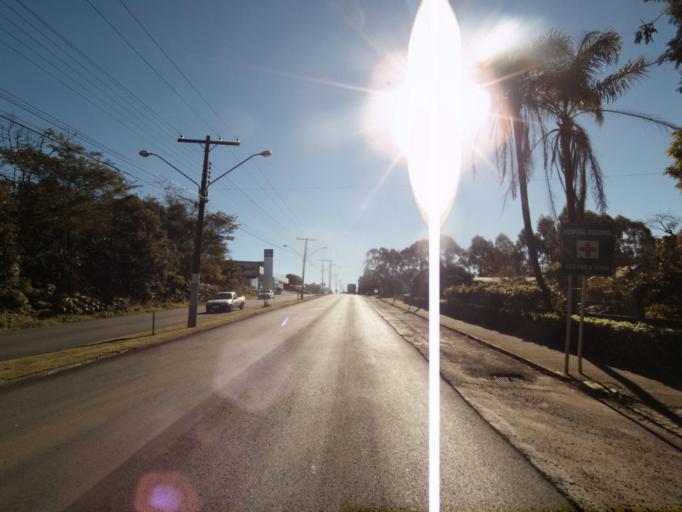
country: AR
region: Misiones
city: Bernardo de Irigoyen
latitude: -26.7353
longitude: -53.5056
